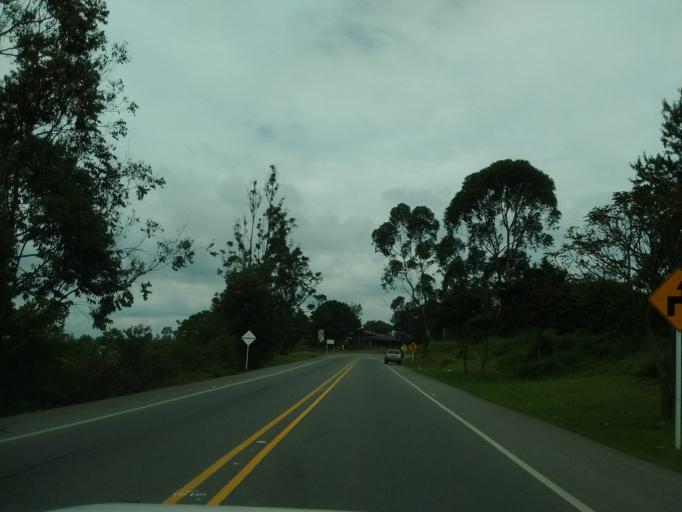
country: CO
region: Cauca
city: Cajibio
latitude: 2.5957
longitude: -76.5270
